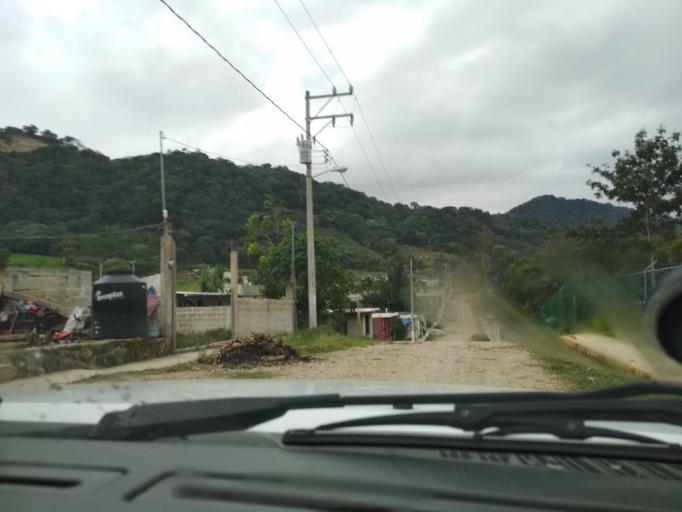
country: MX
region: Veracruz
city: El Castillo
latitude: 19.5717
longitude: -96.8507
